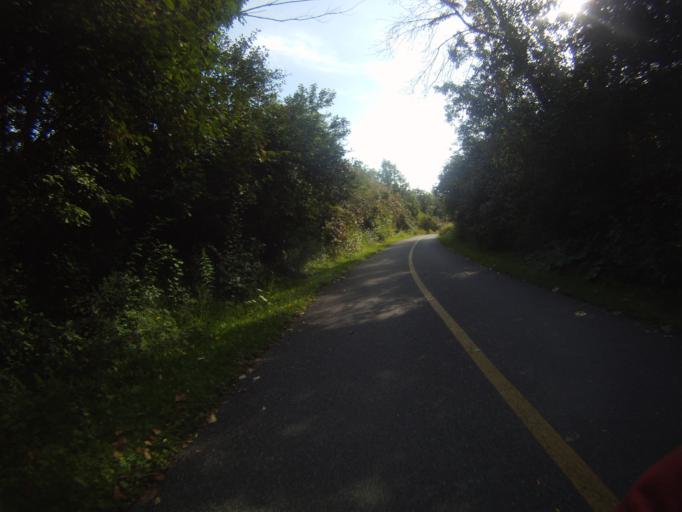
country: CA
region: Ontario
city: Bells Corners
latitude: 45.3419
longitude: -75.8344
